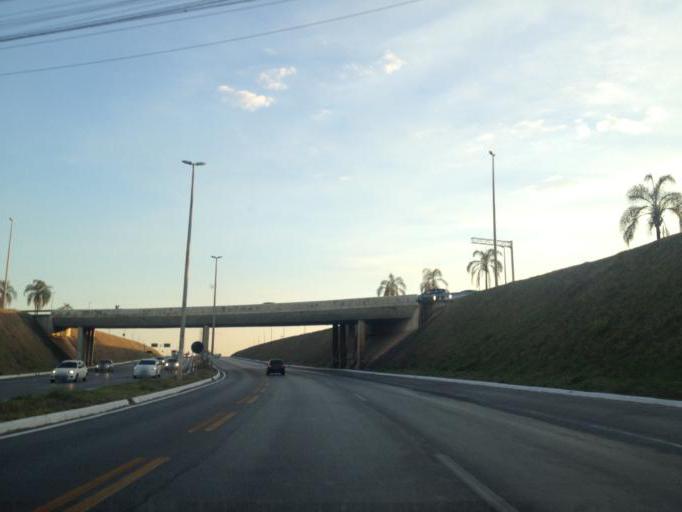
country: BR
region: Federal District
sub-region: Brasilia
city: Brasilia
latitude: -15.7131
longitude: -47.9000
